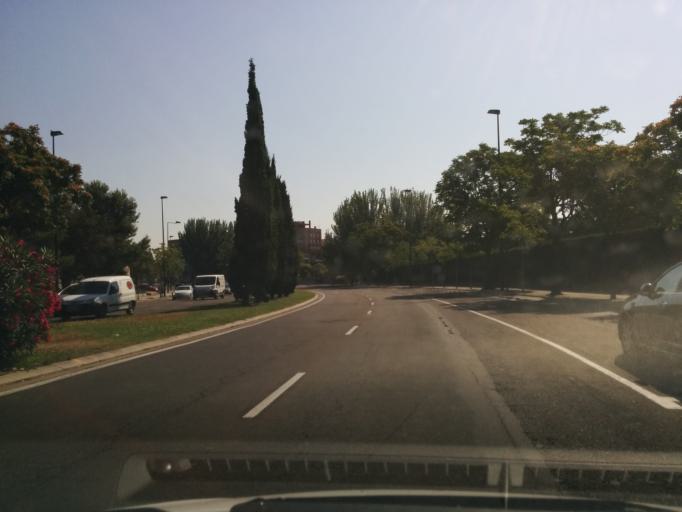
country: ES
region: Aragon
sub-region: Provincia de Zaragoza
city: Zaragoza
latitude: 41.6488
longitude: -0.8660
